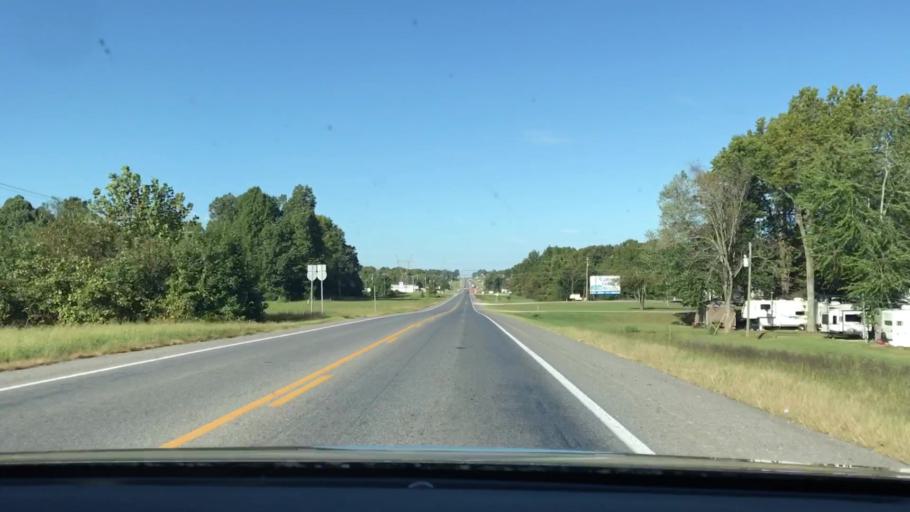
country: US
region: Kentucky
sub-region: Marshall County
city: Calvert City
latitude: 37.0033
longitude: -88.3313
